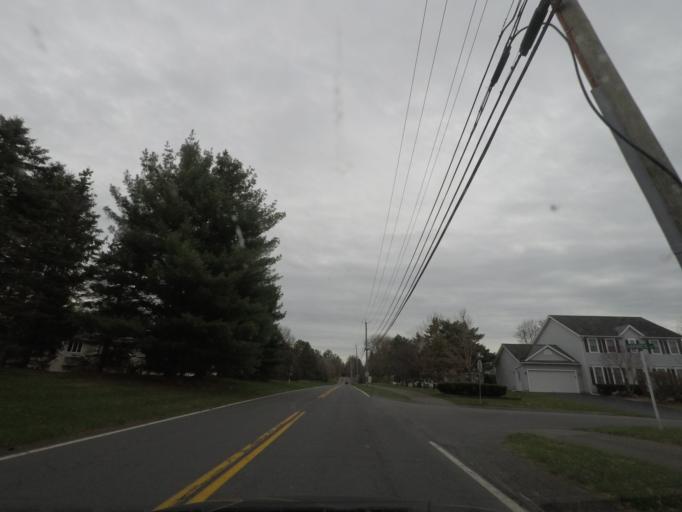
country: US
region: New York
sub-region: Albany County
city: Delmar
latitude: 42.5951
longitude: -73.8112
